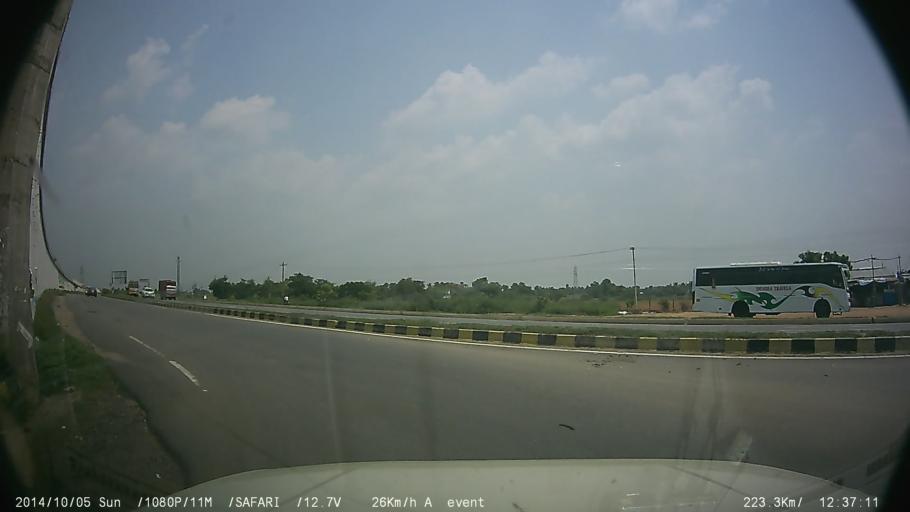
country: IN
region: Tamil Nadu
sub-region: Cuddalore
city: Vriddhachalam
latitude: 11.6774
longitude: 79.2732
